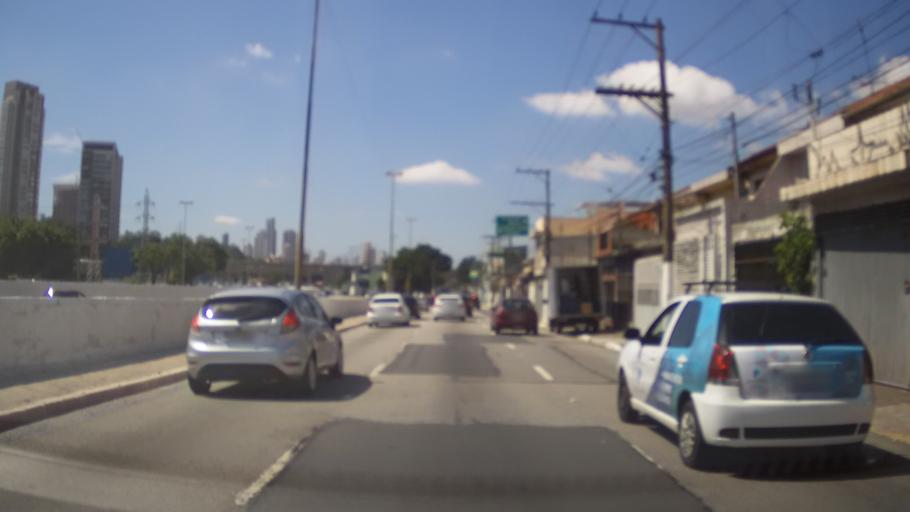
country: BR
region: Sao Paulo
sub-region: Sao Paulo
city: Sao Paulo
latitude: -23.5369
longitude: -46.5818
